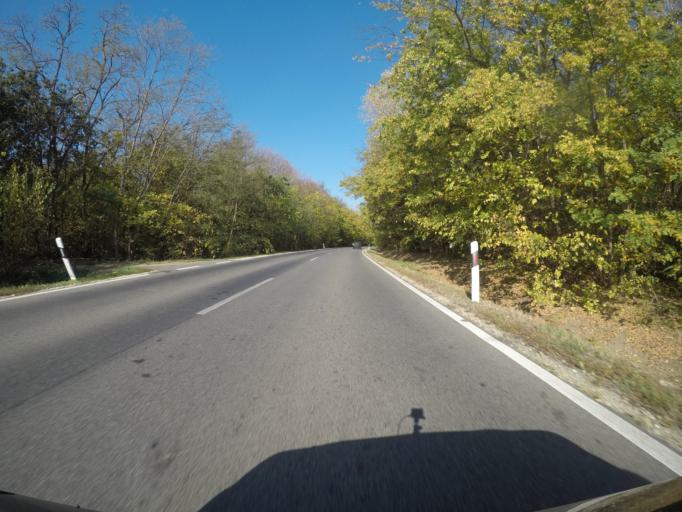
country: HU
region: Tolna
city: Tengelic
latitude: 46.5389
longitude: 18.6532
